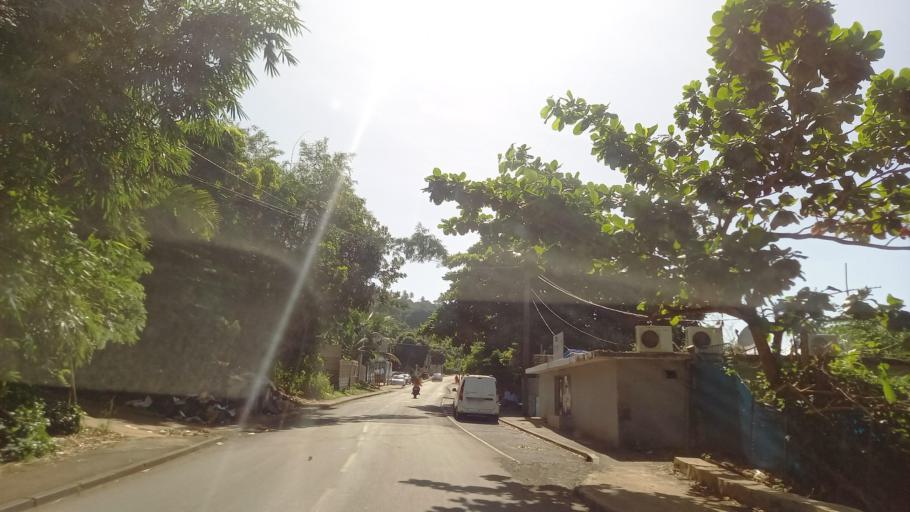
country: YT
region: Bandrele
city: Bandrele
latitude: -12.8945
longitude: 45.2008
